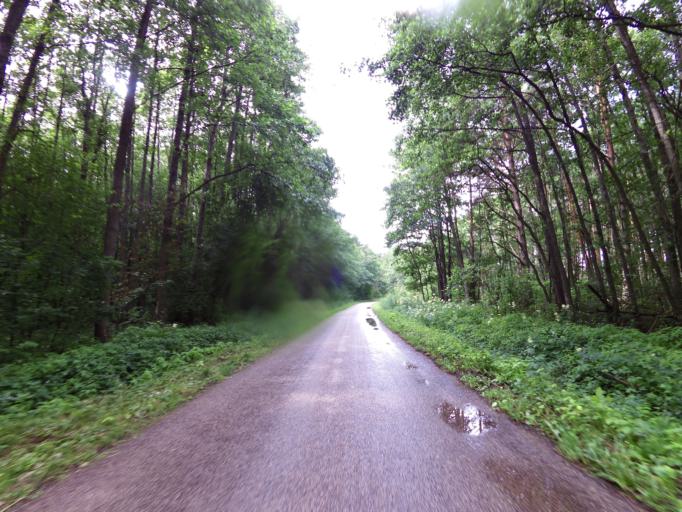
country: EE
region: Laeaene
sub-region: Vormsi vald
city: Hullo
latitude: 58.9959
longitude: 23.3378
